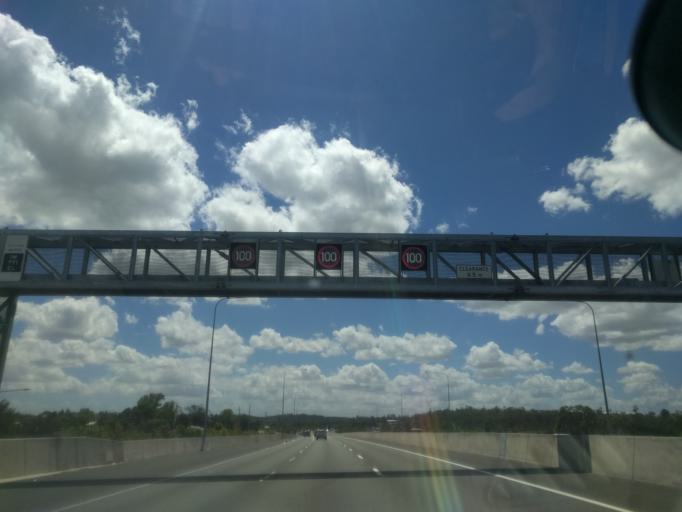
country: AU
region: Queensland
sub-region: Ipswich
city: Redbank
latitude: -27.6039
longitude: 152.8680
